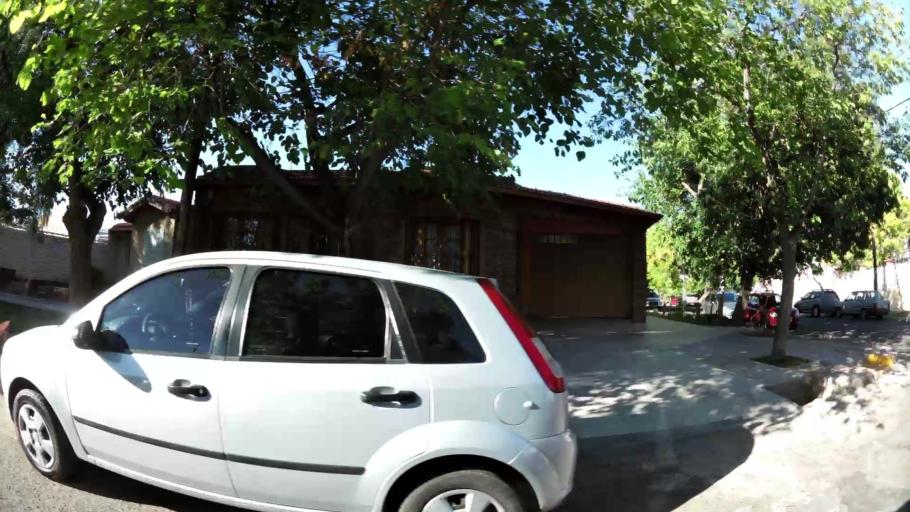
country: AR
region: Mendoza
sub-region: Departamento de Godoy Cruz
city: Godoy Cruz
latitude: -32.9383
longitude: -68.8354
